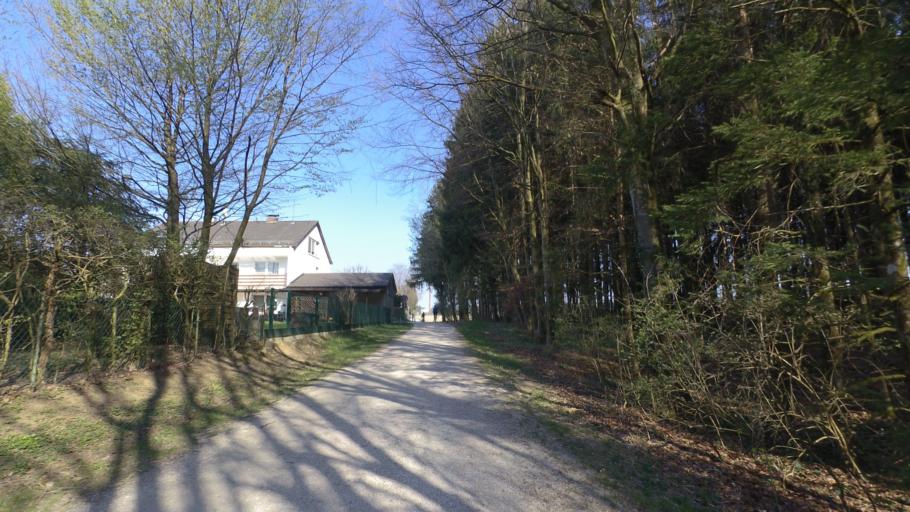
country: DE
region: Bavaria
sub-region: Upper Bavaria
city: Traunreut
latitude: 47.9563
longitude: 12.5928
